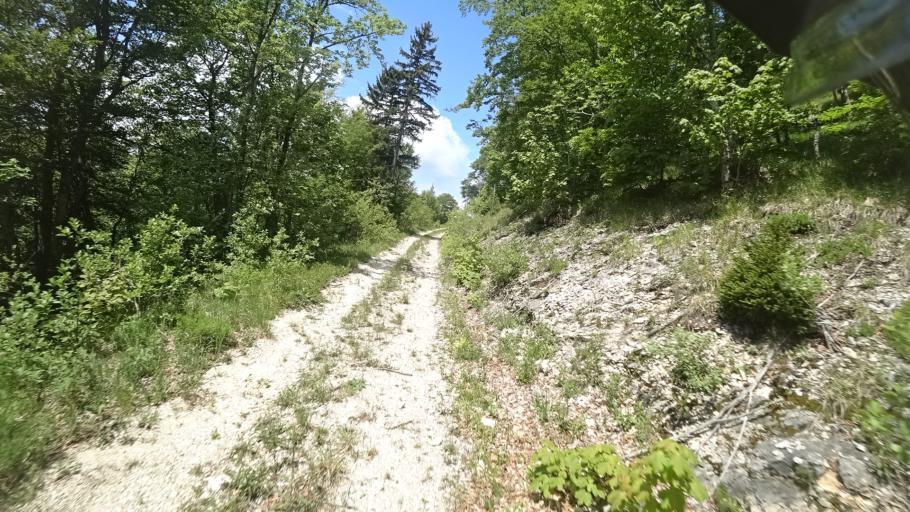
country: BA
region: Federation of Bosnia and Herzegovina
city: Orasac
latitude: 44.5659
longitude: 15.8579
